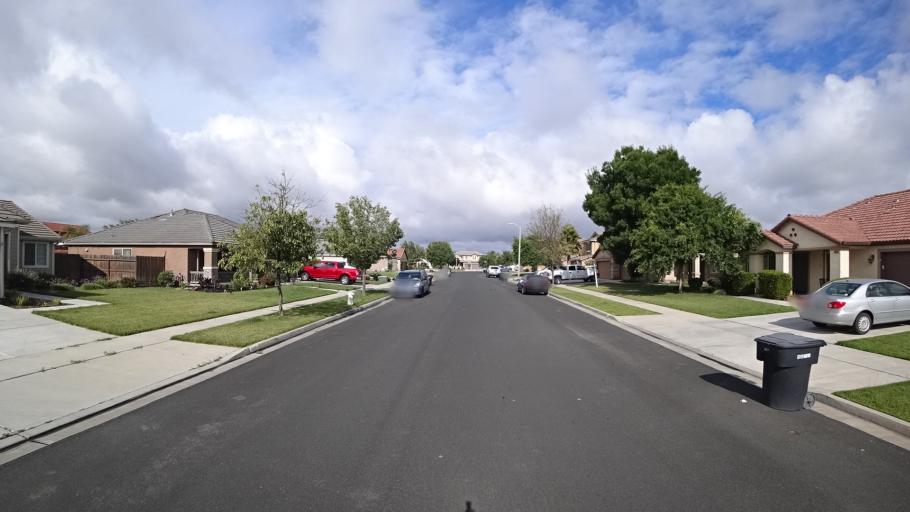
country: US
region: California
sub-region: Kings County
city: Lucerne
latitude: 36.3503
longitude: -119.6664
